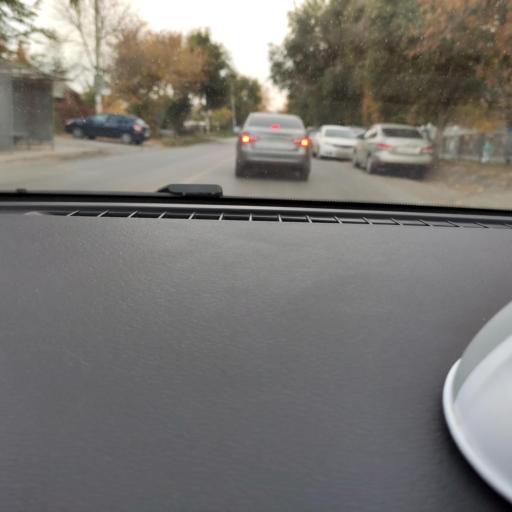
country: RU
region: Samara
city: Samara
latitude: 53.1760
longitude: 50.1705
